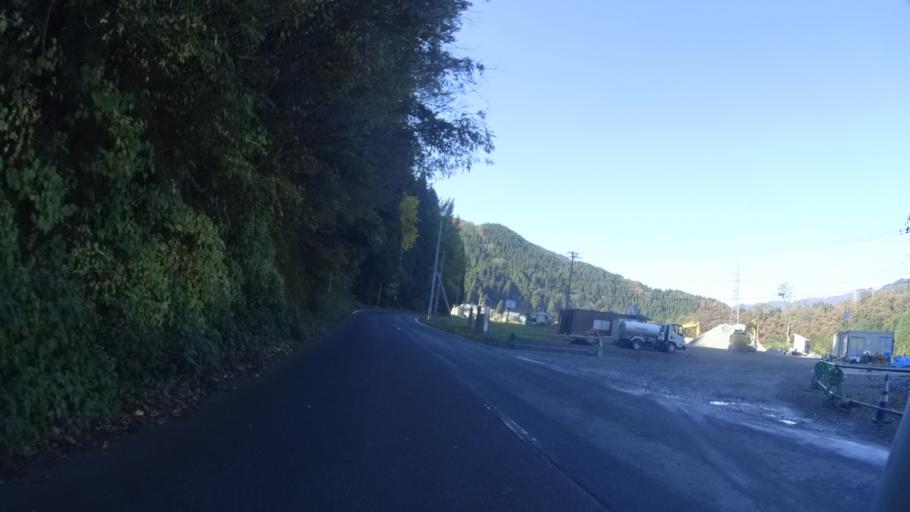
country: JP
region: Fukui
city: Ono
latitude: 35.9846
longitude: 136.3635
